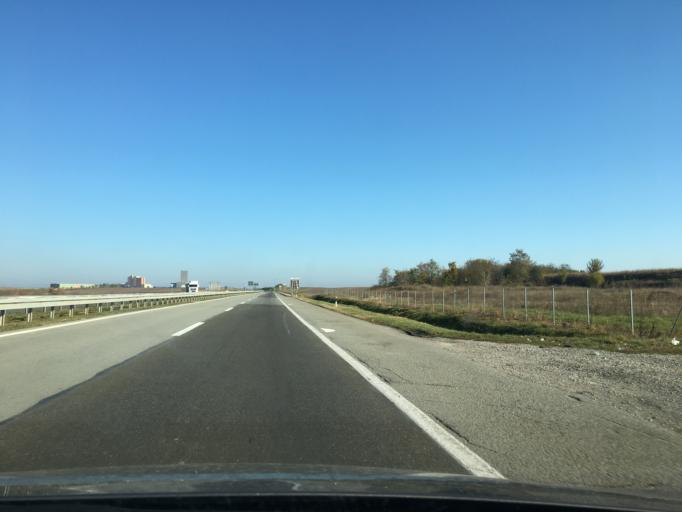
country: RS
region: Autonomna Pokrajina Vojvodina
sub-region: Severnobacki Okrug
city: Mali Igos
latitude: 45.6447
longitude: 19.7158
